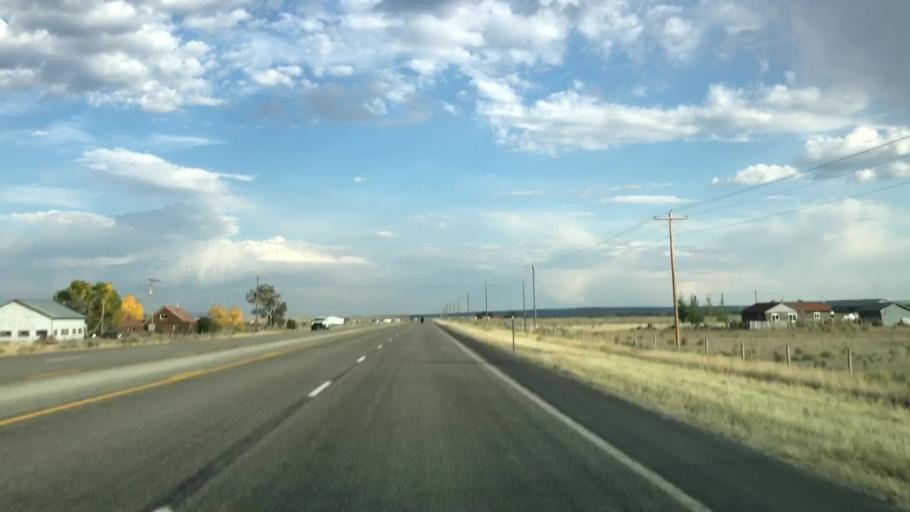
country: US
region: Wyoming
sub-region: Sublette County
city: Pinedale
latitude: 42.7832
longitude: -109.7677
